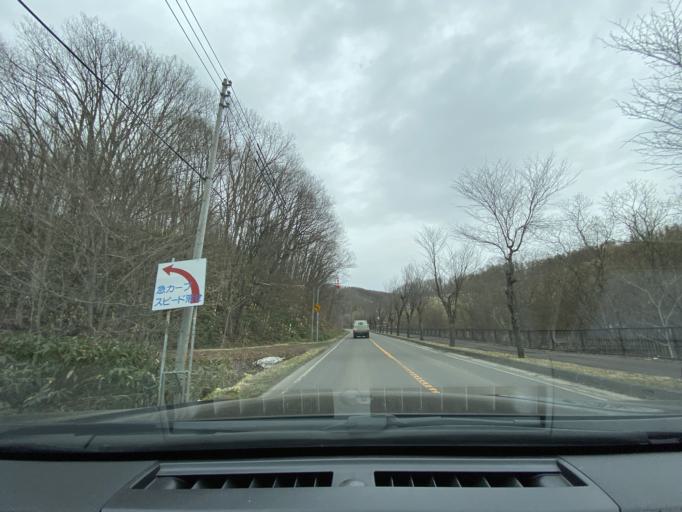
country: JP
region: Hokkaido
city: Nayoro
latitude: 44.0925
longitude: 142.4392
